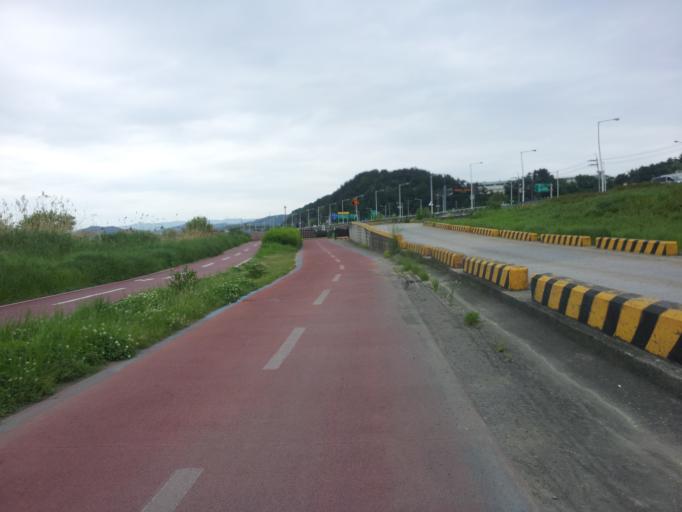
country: KR
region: Daejeon
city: Daejeon
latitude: 36.3580
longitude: 127.4040
